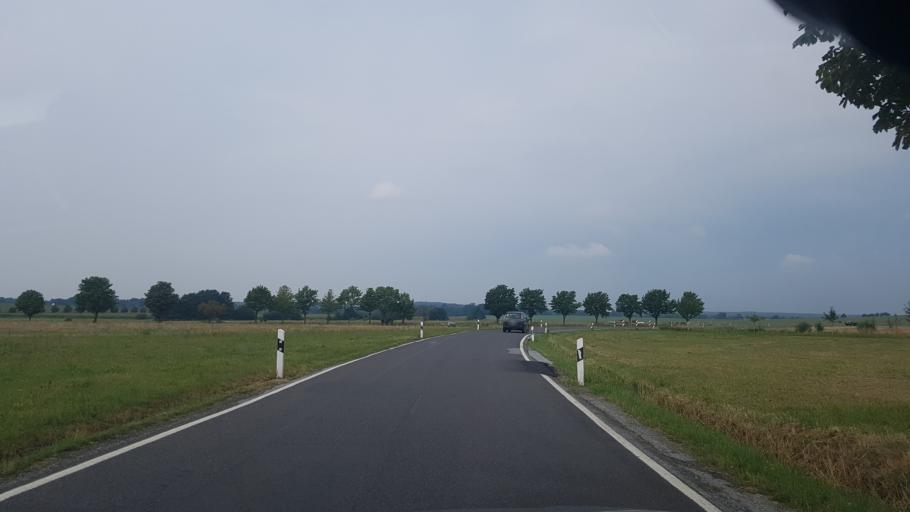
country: DE
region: Saxony
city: Crostwitz
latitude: 51.2426
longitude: 14.2459
